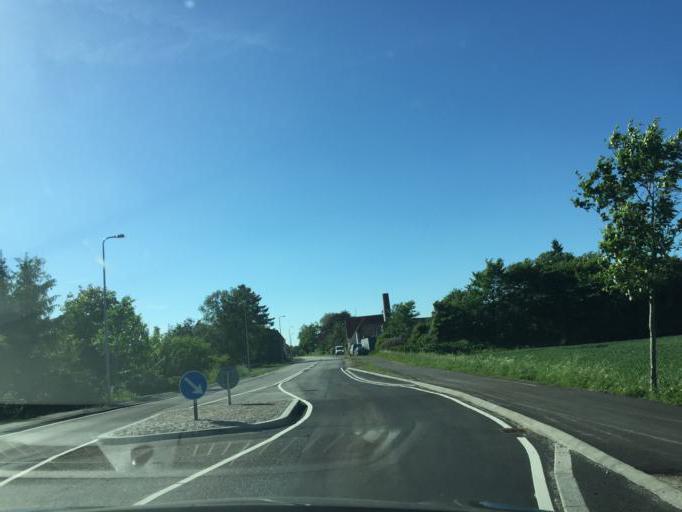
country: DK
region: Zealand
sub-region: Koge Kommune
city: Bjaeverskov
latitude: 55.4257
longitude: 11.9949
